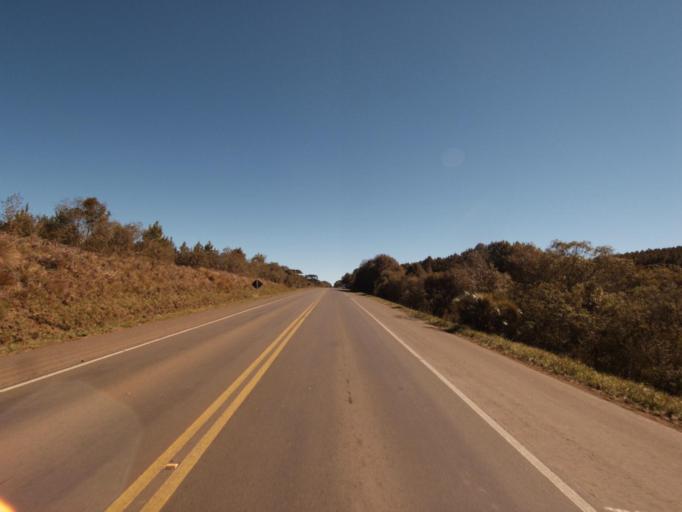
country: BR
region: Santa Catarina
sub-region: Concordia
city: Concordia
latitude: -26.9169
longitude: -51.8934
